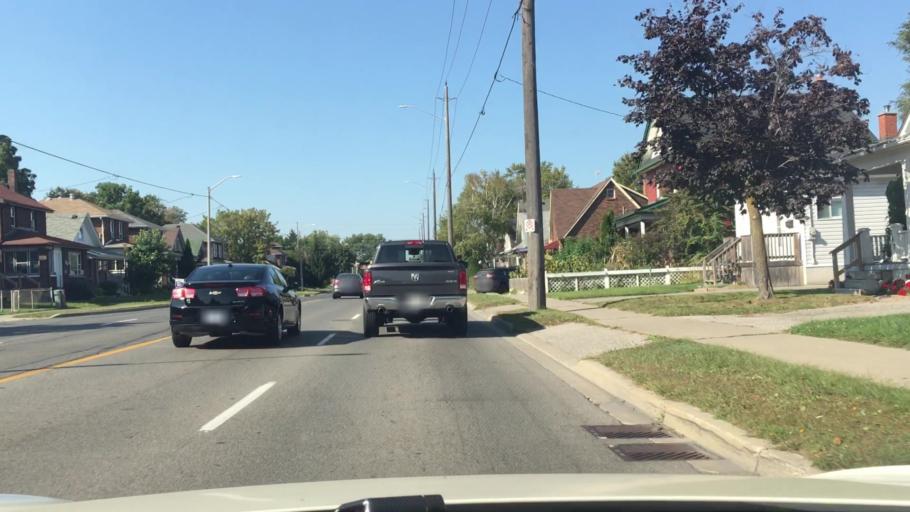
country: CA
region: Ontario
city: Oshawa
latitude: 43.8932
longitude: -78.8507
